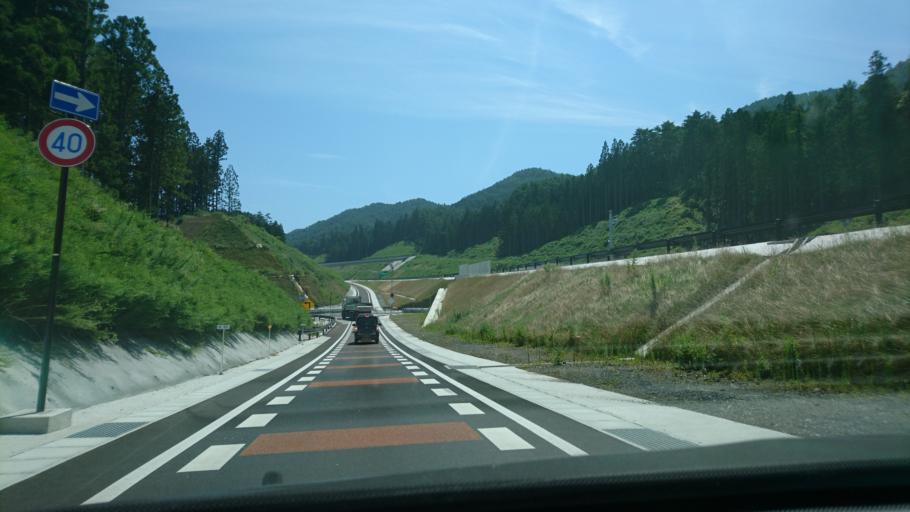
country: JP
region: Iwate
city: Ofunato
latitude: 38.9868
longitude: 141.6128
